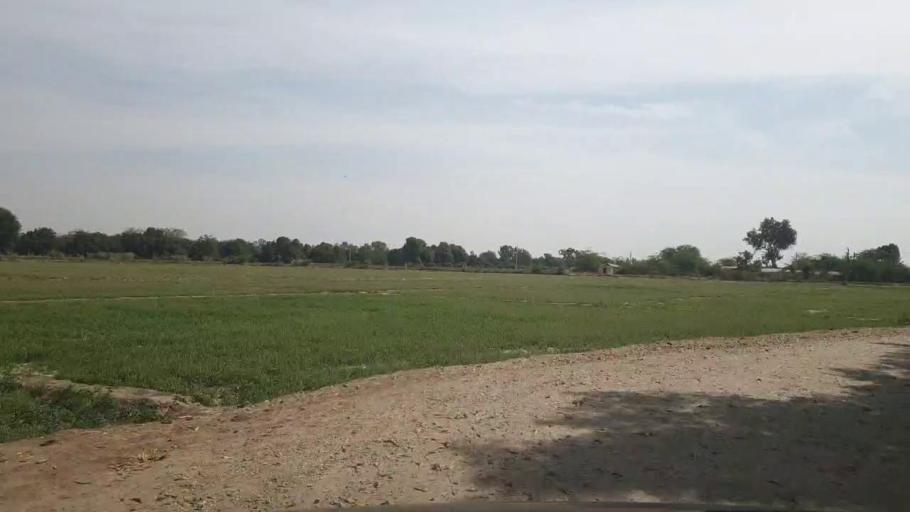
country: PK
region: Sindh
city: Kunri
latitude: 25.2092
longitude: 69.6889
